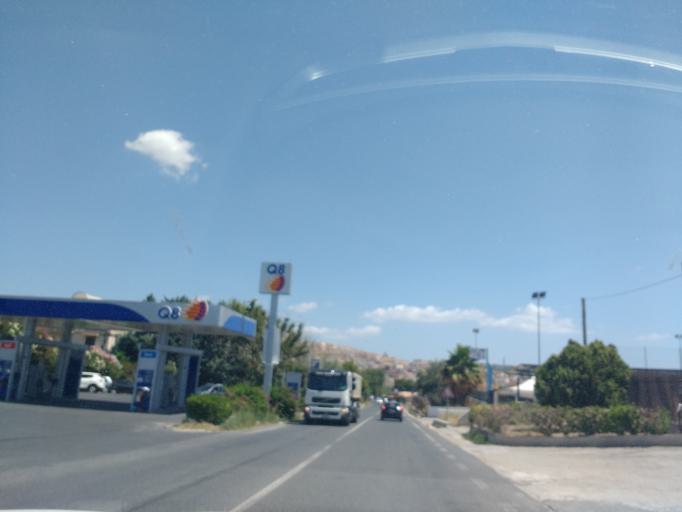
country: IT
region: Sicily
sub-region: Provincia di Siracusa
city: Noto
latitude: 36.8811
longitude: 15.0614
